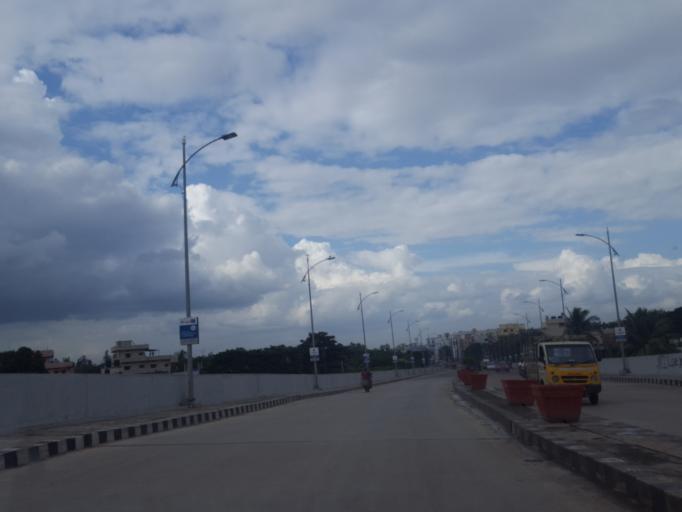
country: IN
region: Telangana
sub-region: Medak
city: Serilingampalle
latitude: 17.4829
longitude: 78.3113
